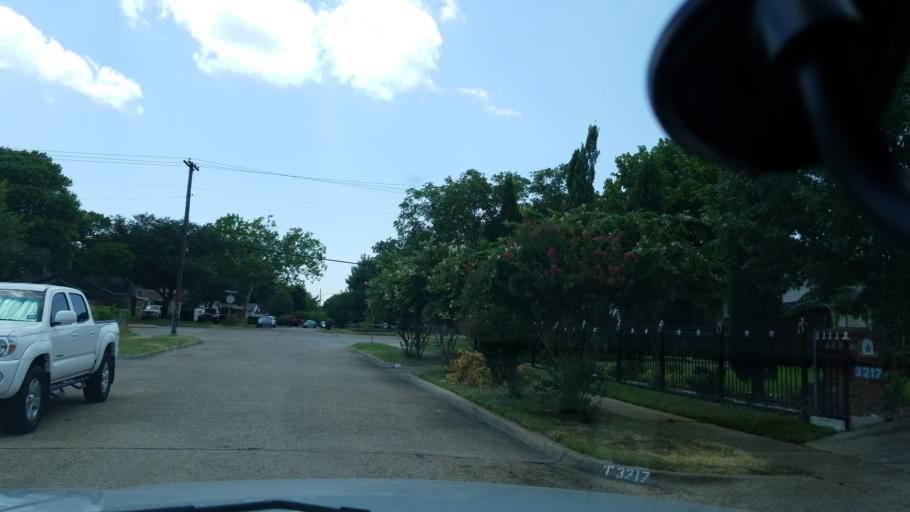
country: US
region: Texas
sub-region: Dallas County
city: Cockrell Hill
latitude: 32.7254
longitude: -96.8737
